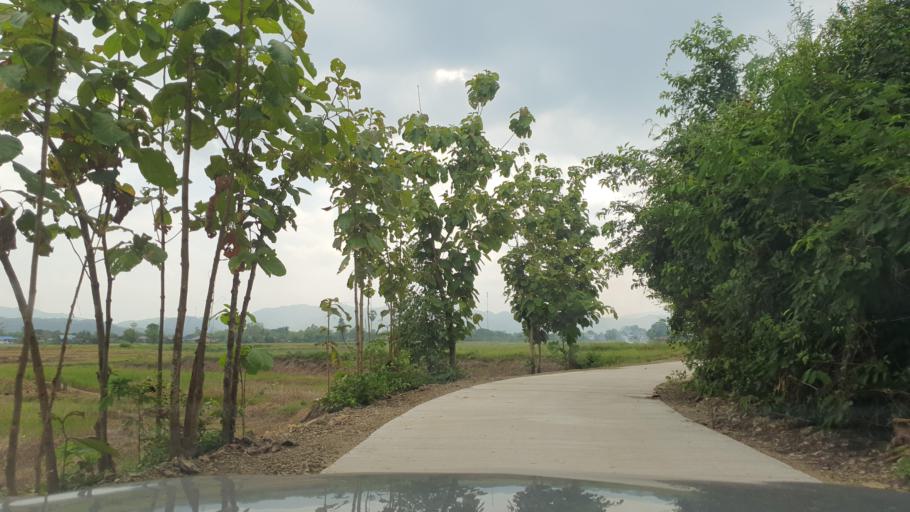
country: TH
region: Sukhothai
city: Thung Saliam
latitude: 17.3296
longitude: 99.4523
